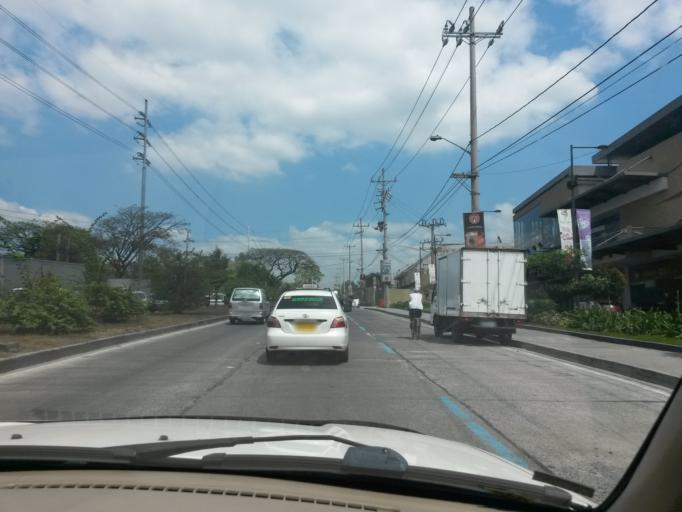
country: PH
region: Metro Manila
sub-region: Quezon City
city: Quezon City
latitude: 14.6496
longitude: 121.0746
